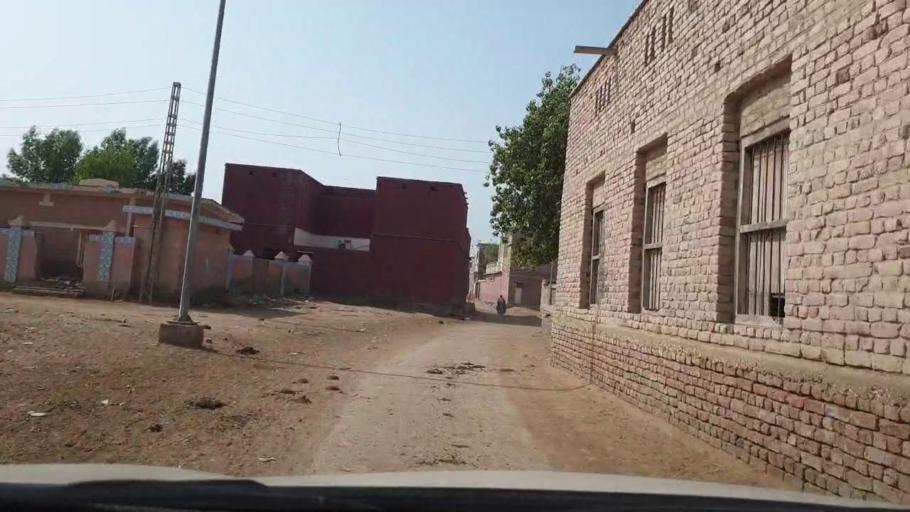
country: PK
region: Sindh
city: Larkana
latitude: 27.4600
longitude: 68.2303
